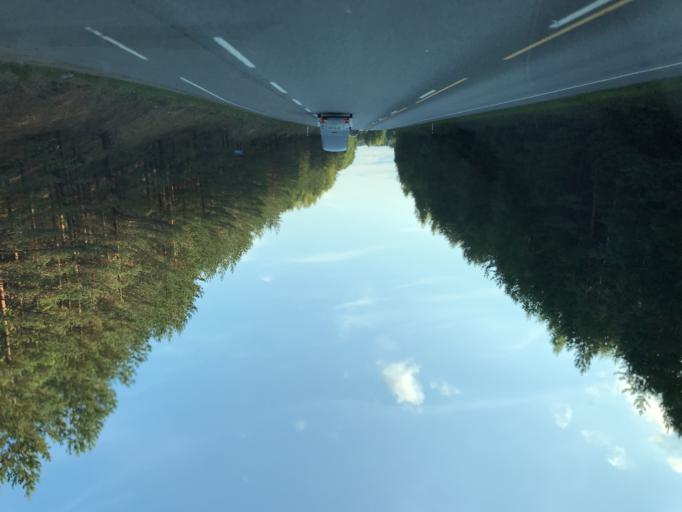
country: FI
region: Uusimaa
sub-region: Helsinki
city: Vihti
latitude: 60.3592
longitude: 24.3254
